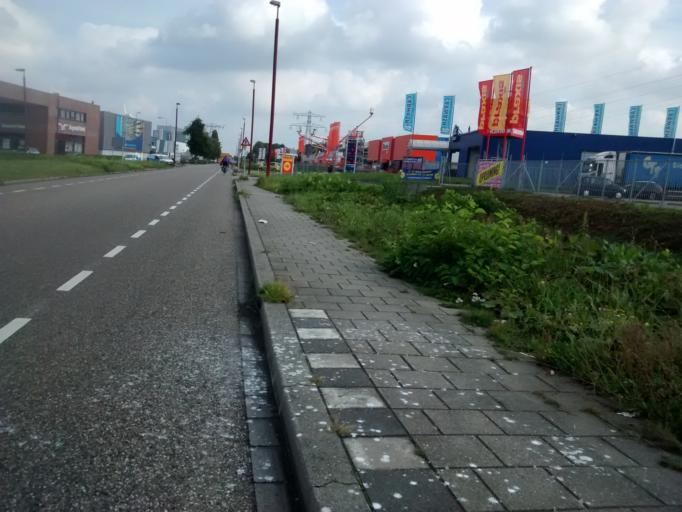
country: NL
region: Utrecht
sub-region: Gemeente Utrecht
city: Lunetten
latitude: 52.0507
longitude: 5.1105
